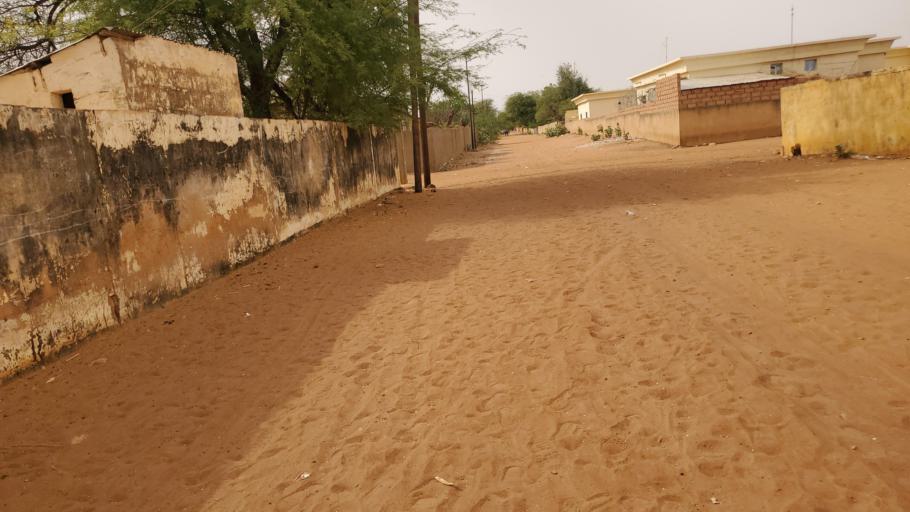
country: SN
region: Louga
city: Ndibene Dahra
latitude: 15.3966
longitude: -15.1149
